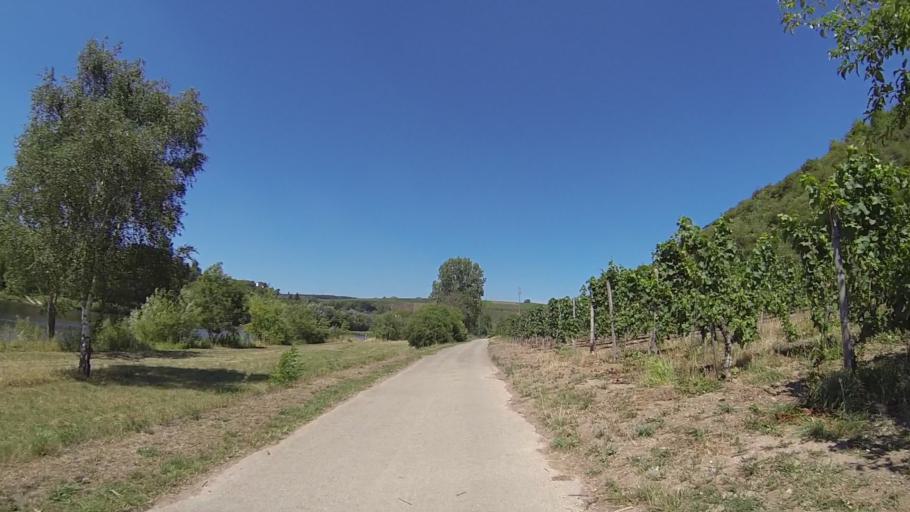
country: LU
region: Grevenmacher
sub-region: Canton de Remich
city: Lenningen
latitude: 49.5843
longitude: 6.3790
